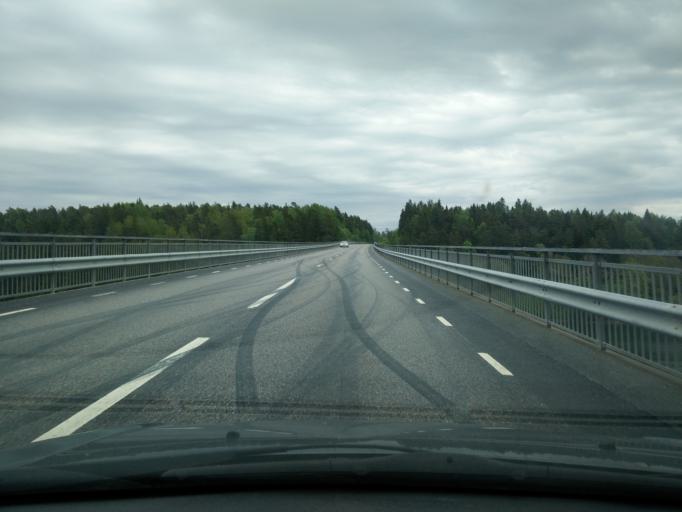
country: SE
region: Stockholm
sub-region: Norrtalje Kommun
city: Bjorko
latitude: 59.8197
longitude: 18.9151
